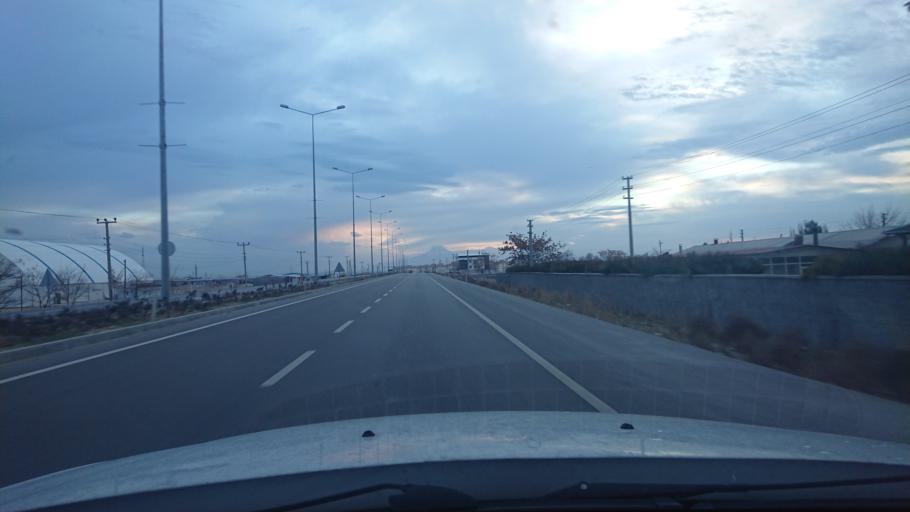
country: TR
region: Aksaray
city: Sultanhani
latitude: 38.2533
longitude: 33.5606
